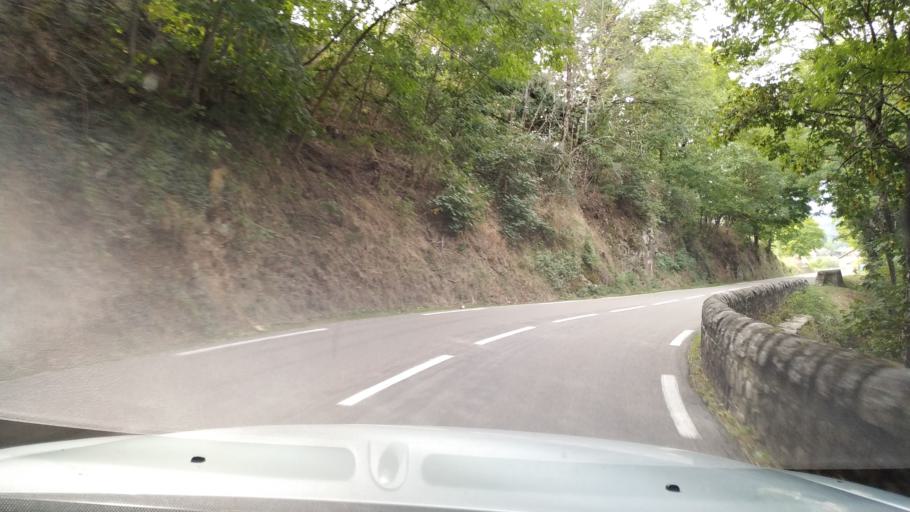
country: FR
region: Rhone-Alpes
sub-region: Departement de l'Ardeche
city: Desaignes
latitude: 44.9942
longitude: 4.5247
